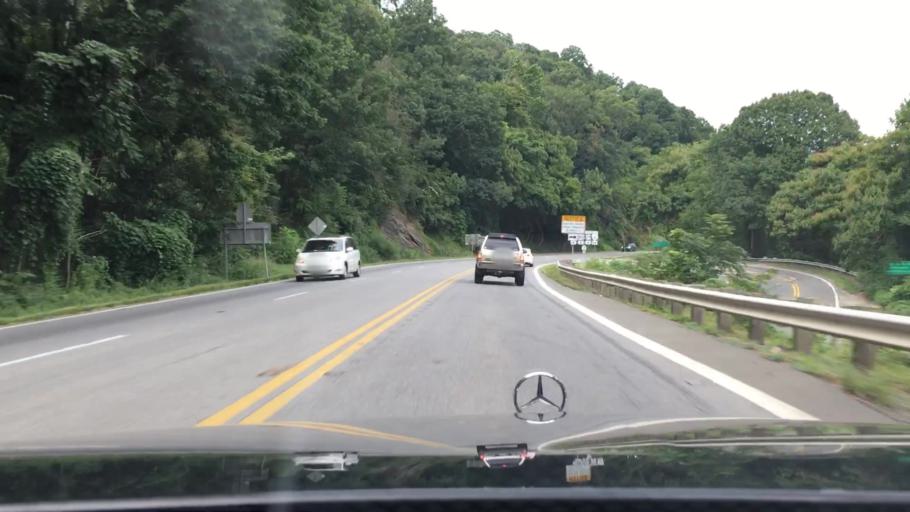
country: US
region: Virginia
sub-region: City of Waynesboro
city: Waynesboro
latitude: 38.0373
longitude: -78.8378
